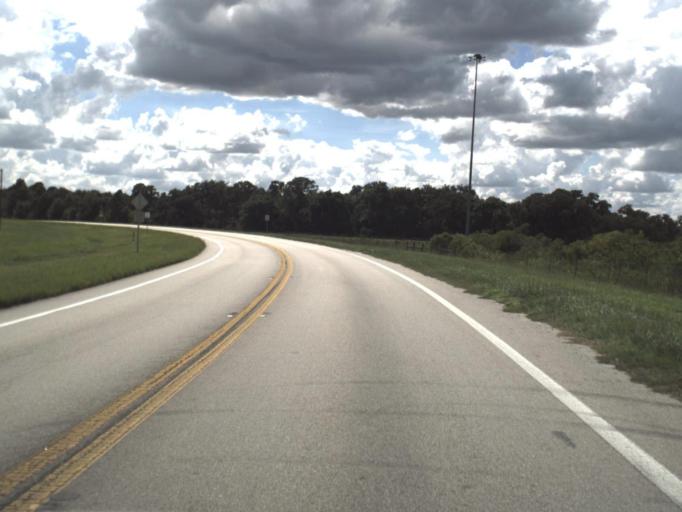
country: US
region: Florida
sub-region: Polk County
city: Fussels Corner
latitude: 28.0090
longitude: -81.8435
